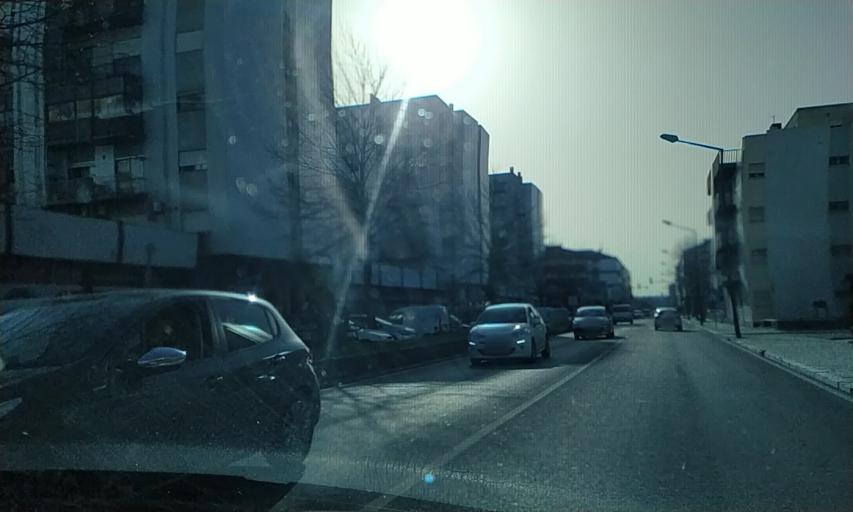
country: PT
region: Leiria
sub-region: Marinha Grande
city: Marinha Grande
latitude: 39.7485
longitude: -8.9264
